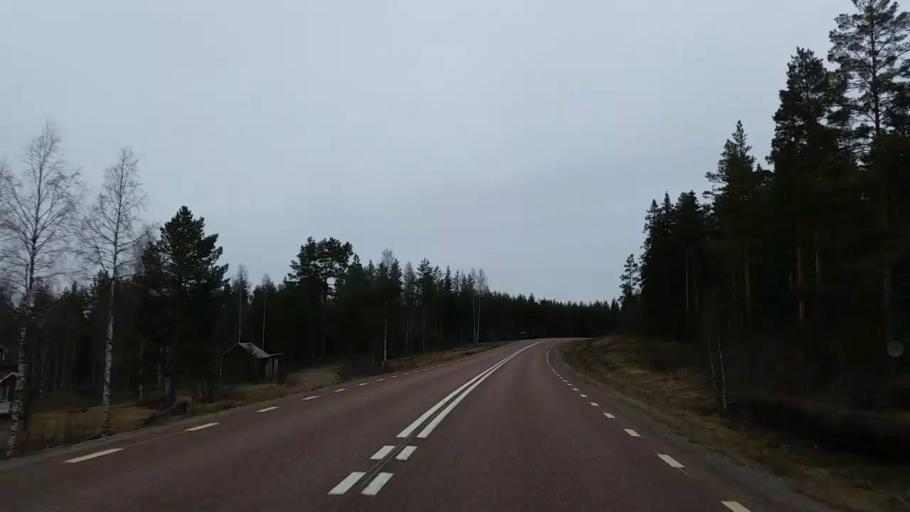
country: SE
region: Gaevleborg
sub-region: Ovanakers Kommun
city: Edsbyn
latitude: 61.2252
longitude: 15.8765
